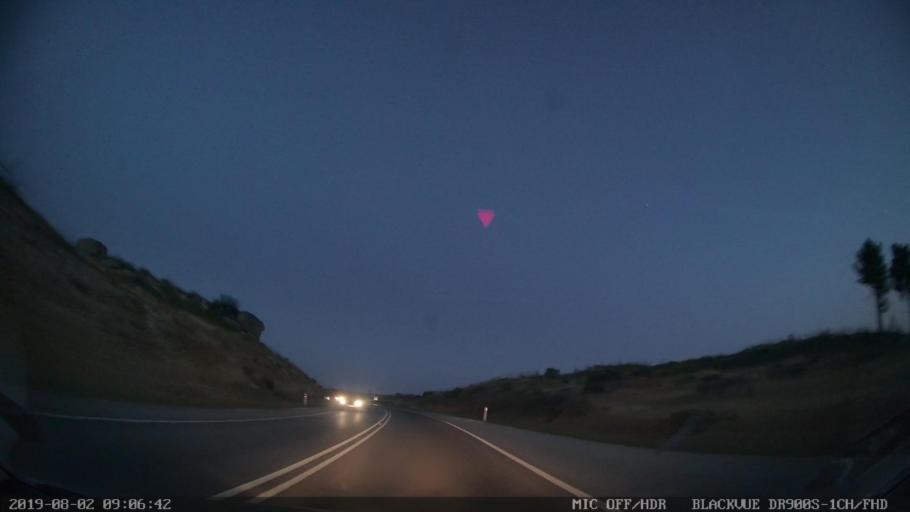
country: PT
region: Portalegre
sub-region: Nisa
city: Nisa
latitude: 39.5236
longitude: -7.7827
